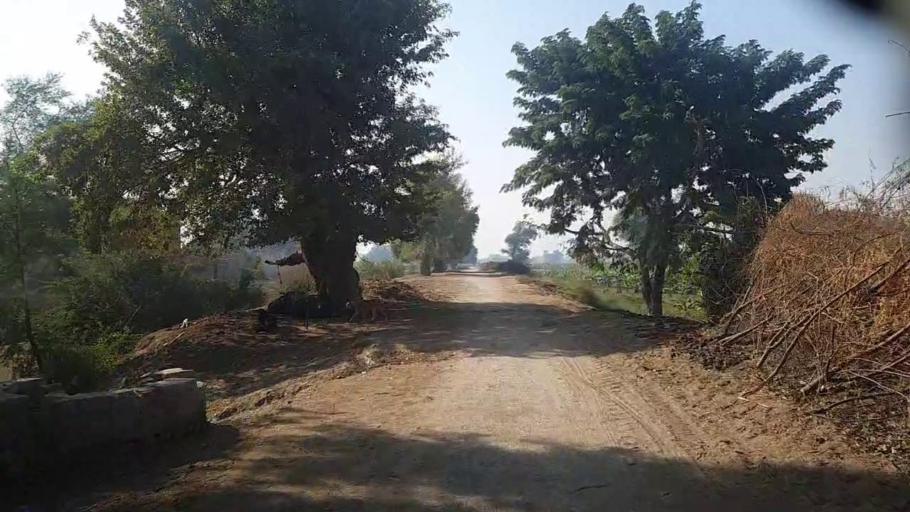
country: PK
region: Sindh
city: Kandiari
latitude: 27.0067
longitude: 68.4957
